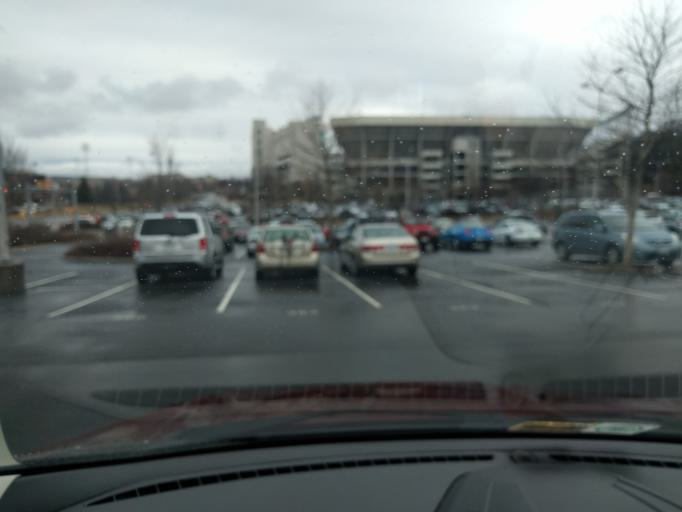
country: US
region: Virginia
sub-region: Montgomery County
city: Blacksburg
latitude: 37.2168
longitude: -80.4185
